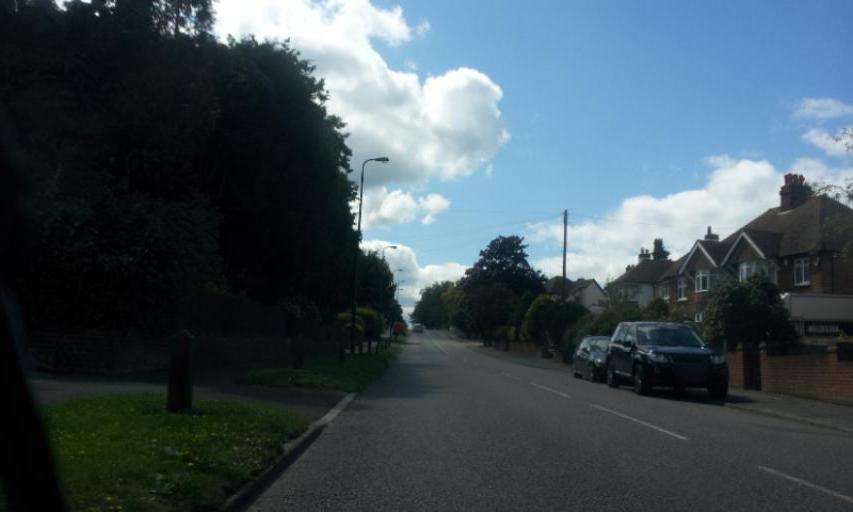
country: GB
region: England
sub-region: Kent
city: Boxley
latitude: 51.2875
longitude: 0.5352
